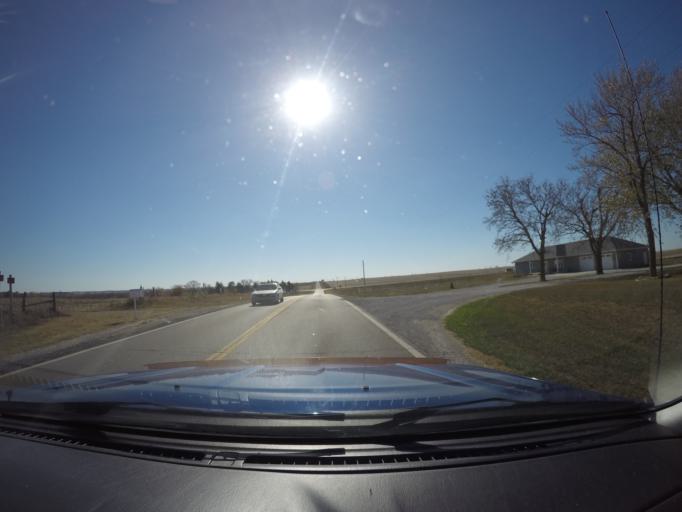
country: US
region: Kansas
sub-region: Nemaha County
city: Seneca
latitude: 39.8442
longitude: -96.2585
